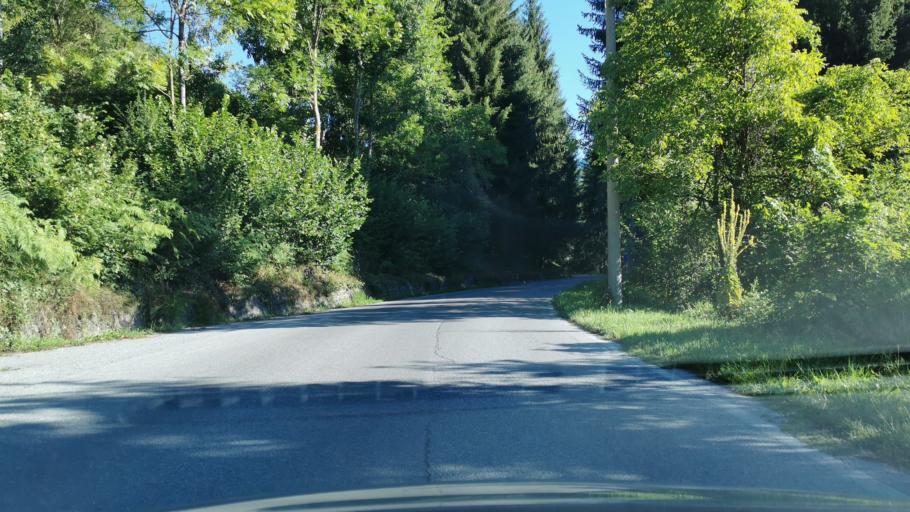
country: IT
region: Piedmont
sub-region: Provincia di Cuneo
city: Entracque
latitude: 44.2292
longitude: 7.3896
